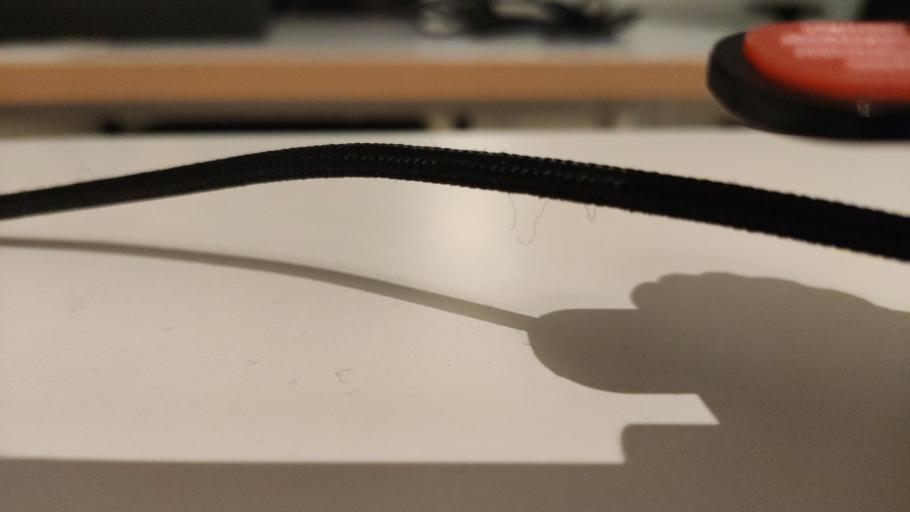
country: RU
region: Moskovskaya
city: Gorshkovo
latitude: 56.3722
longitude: 37.4200
